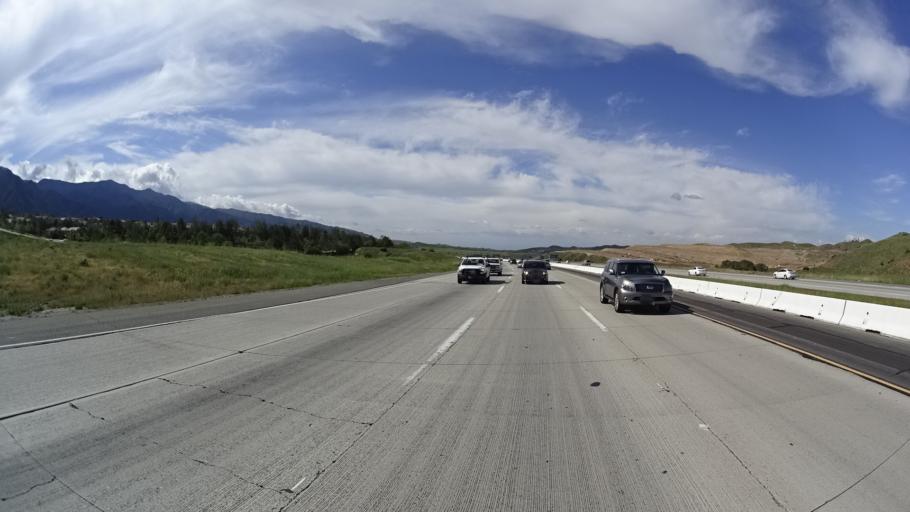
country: US
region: California
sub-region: Riverside County
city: El Cerrito
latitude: 33.7528
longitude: -117.4562
